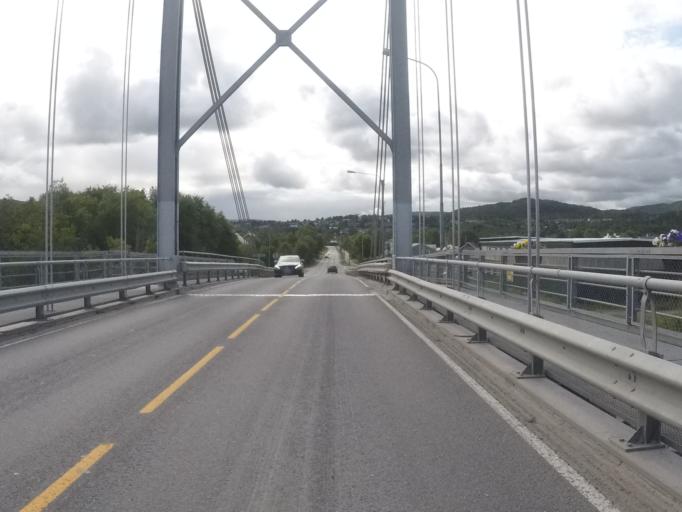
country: NO
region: Finnmark Fylke
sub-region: Alta
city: Alta
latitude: 69.9682
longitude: 23.3753
